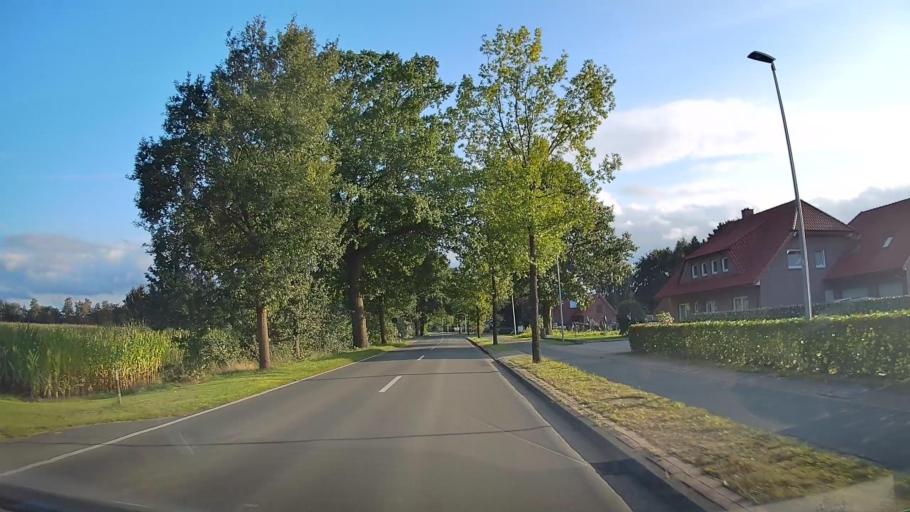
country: DE
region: Lower Saxony
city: Hilkenbrook
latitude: 53.0319
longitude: 7.7460
